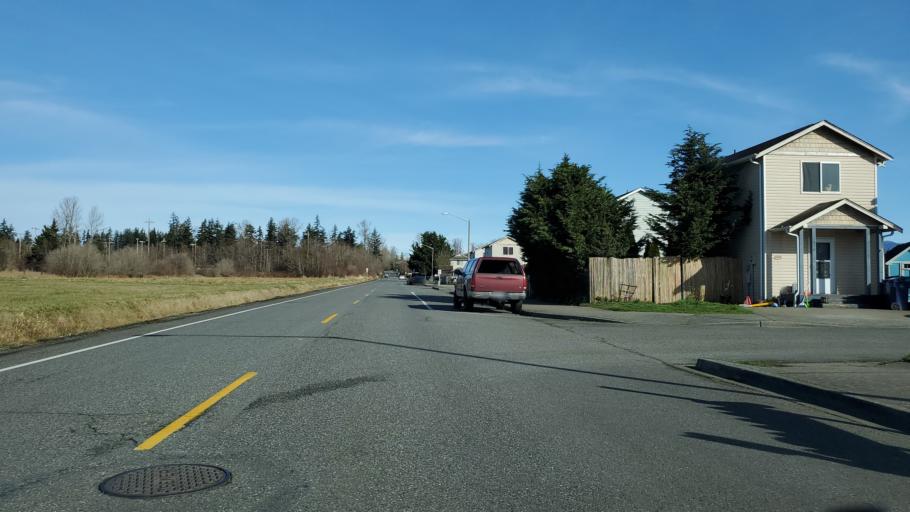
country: US
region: Washington
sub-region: Skagit County
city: Mount Vernon
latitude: 48.4368
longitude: -122.3026
